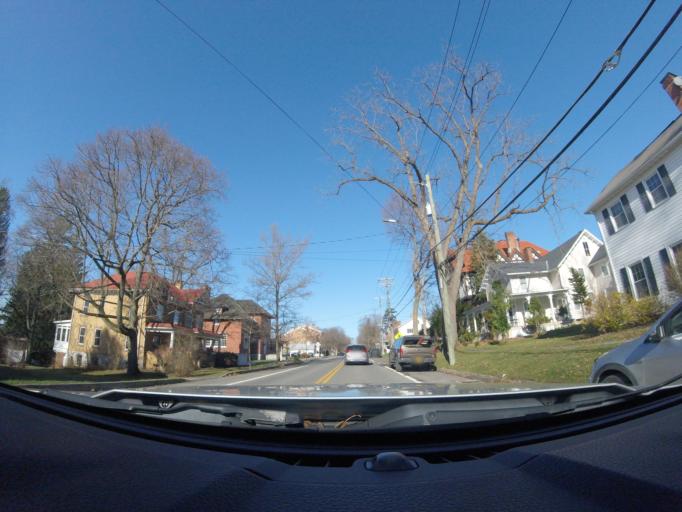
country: US
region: New York
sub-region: Cayuga County
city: Union Springs
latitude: 42.7533
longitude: -76.7022
